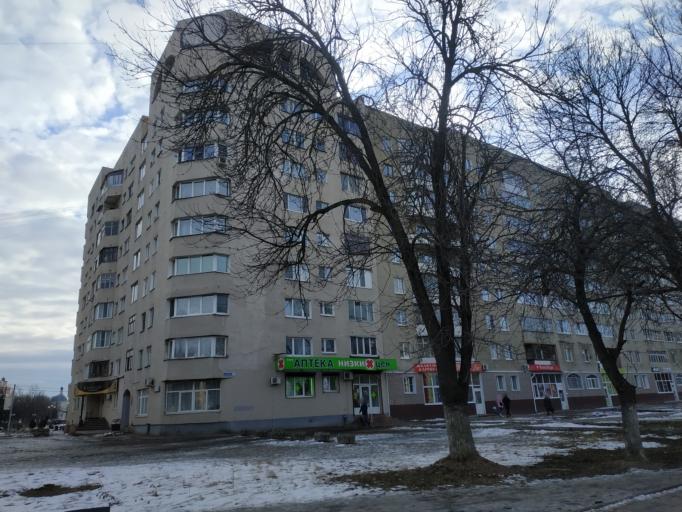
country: RU
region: Tverskaya
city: Tver
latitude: 56.8544
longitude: 35.9266
